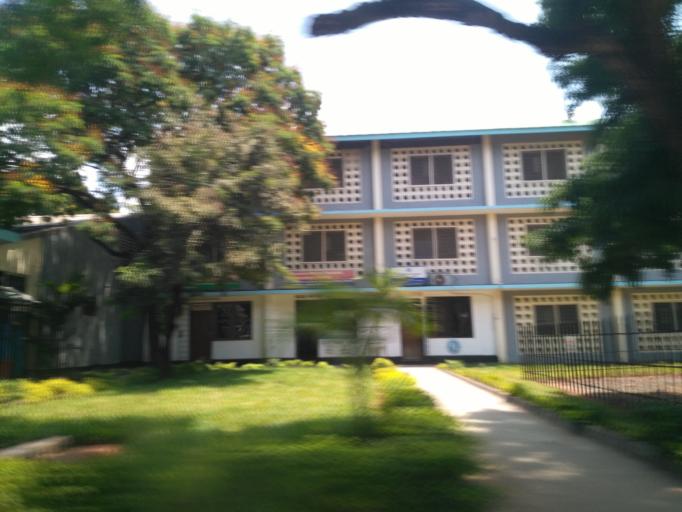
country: TZ
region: Dar es Salaam
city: Dar es Salaam
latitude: -6.8069
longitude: 39.2732
